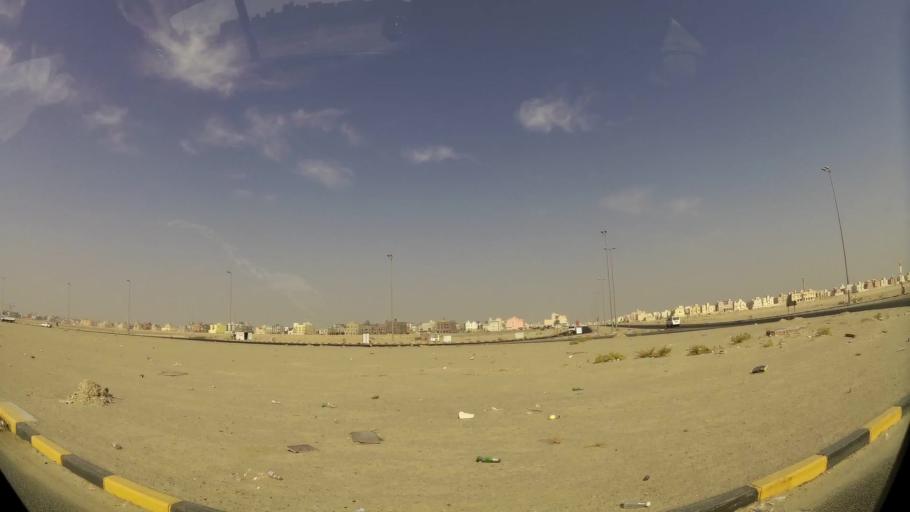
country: KW
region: Al Ahmadi
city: Al Wafrah
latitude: 28.7834
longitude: 48.0698
